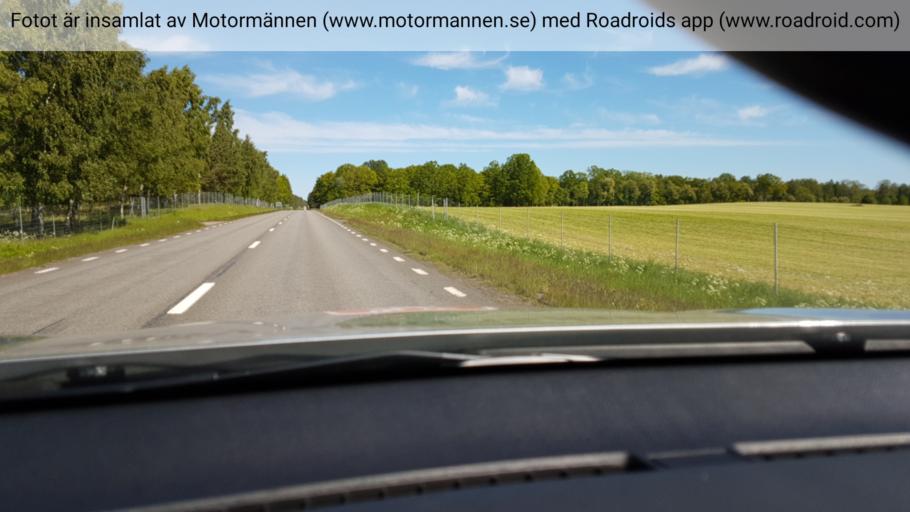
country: SE
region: Vaestra Goetaland
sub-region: Hjo Kommun
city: Hjo
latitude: 58.3613
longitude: 14.3526
